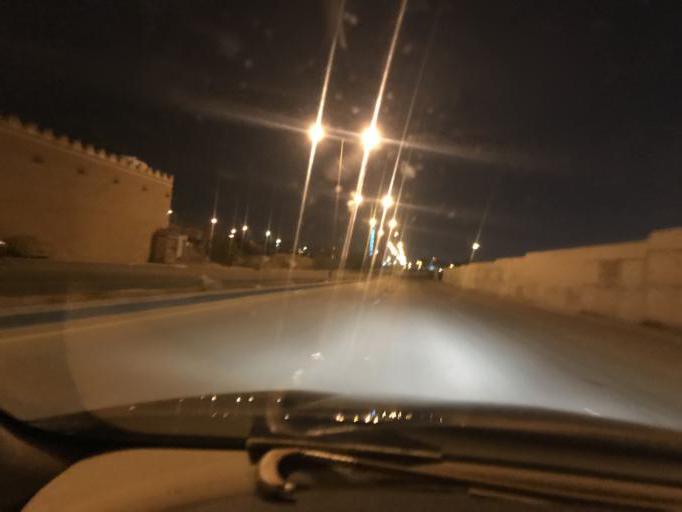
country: SA
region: Ar Riyad
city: Riyadh
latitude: 24.8159
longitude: 46.7179
